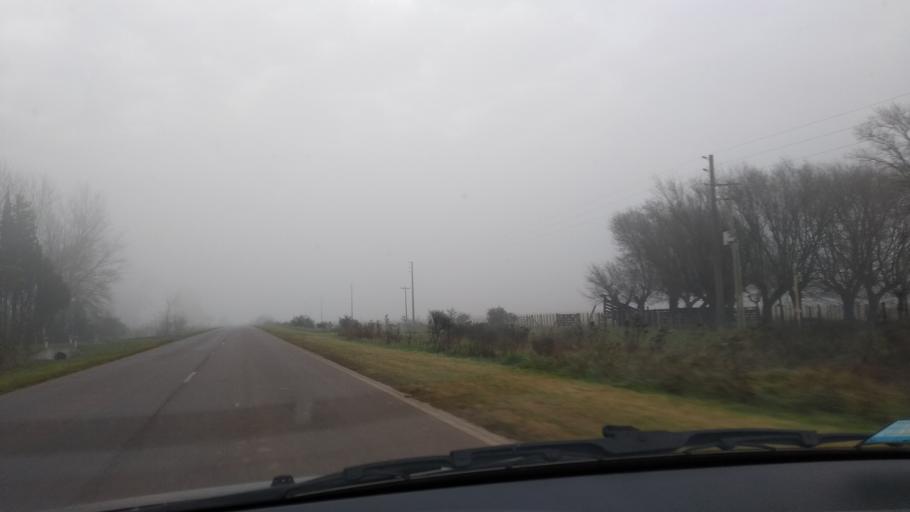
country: AR
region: Buenos Aires
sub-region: Partido de San Vicente
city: San Vicente
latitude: -35.2380
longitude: -58.4699
